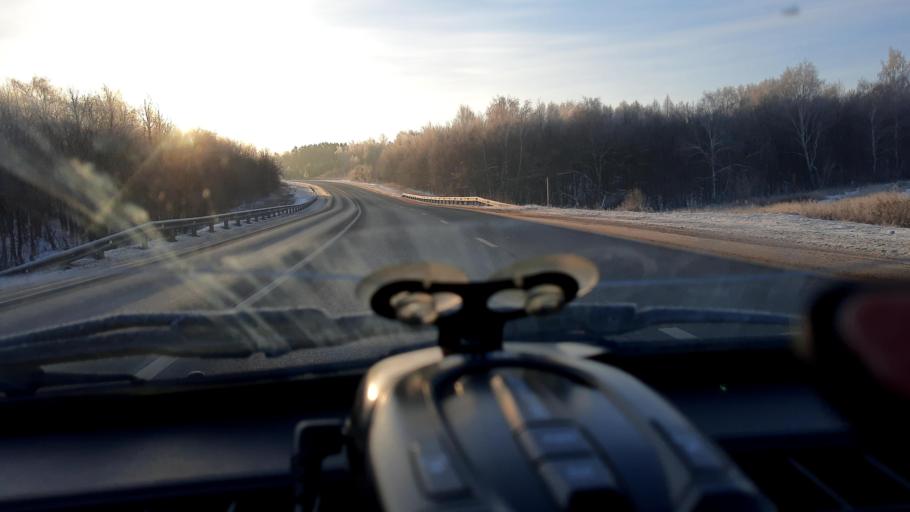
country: RU
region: Bashkortostan
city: Avdon
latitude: 54.8512
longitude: 55.7044
